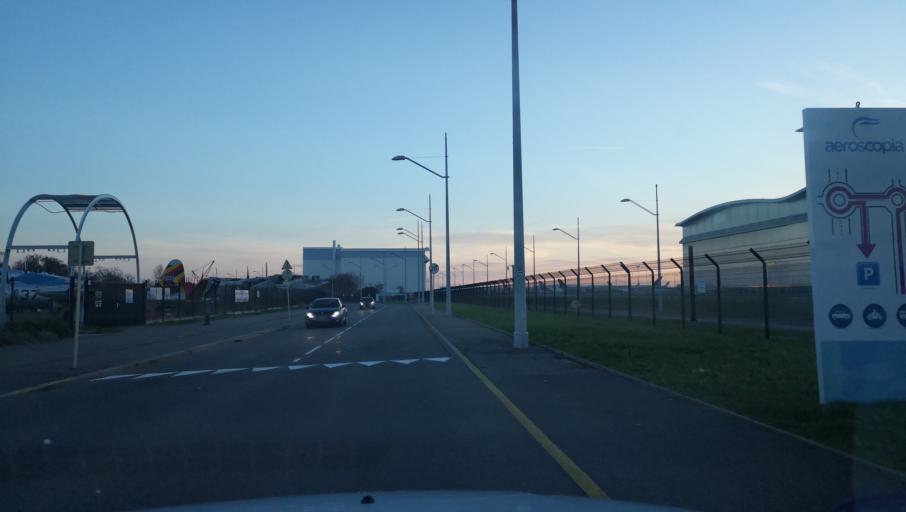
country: FR
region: Midi-Pyrenees
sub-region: Departement de la Haute-Garonne
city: Beauzelle
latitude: 43.6582
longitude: 1.3585
